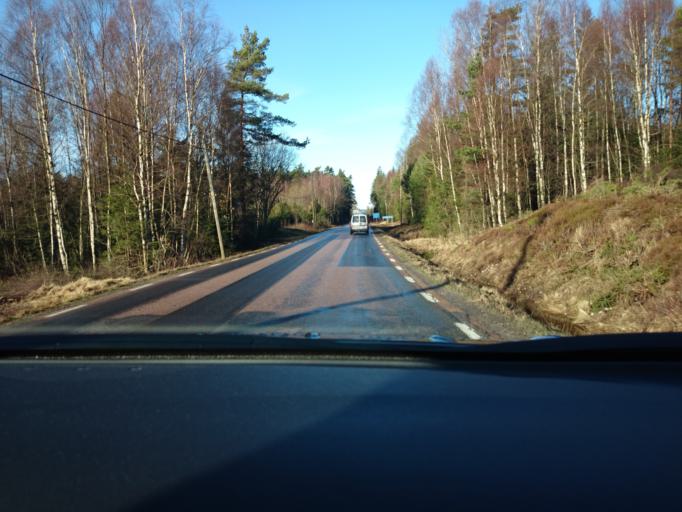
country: SE
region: Halland
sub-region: Hylte Kommun
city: Hyltebruk
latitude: 57.0226
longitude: 13.2314
